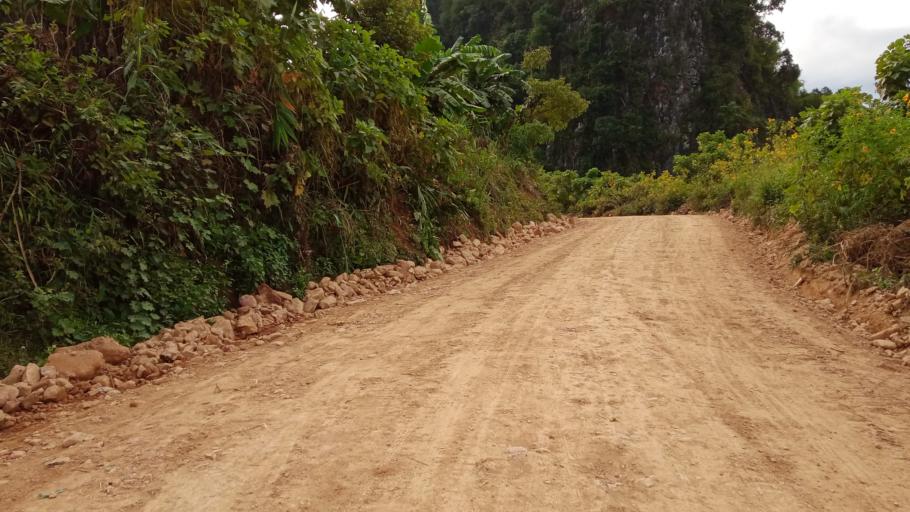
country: LA
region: Xiangkhoang
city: Phonsavan
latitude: 19.1184
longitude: 102.9153
